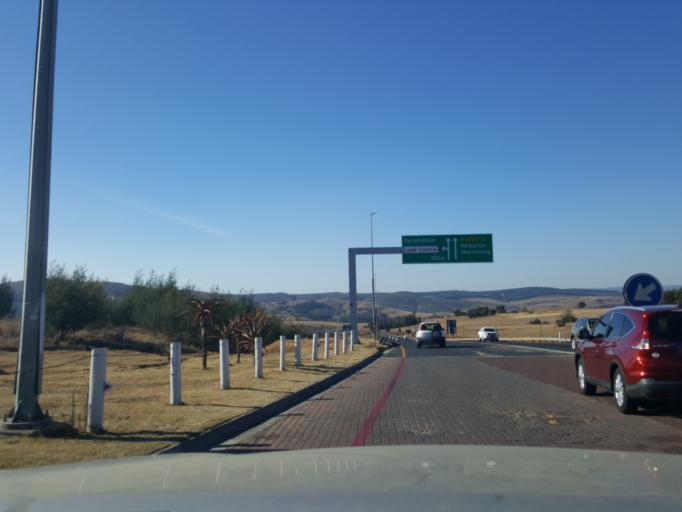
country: ZA
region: Mpumalanga
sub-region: Nkangala District Municipality
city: Belfast
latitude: -25.6269
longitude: 30.2590
